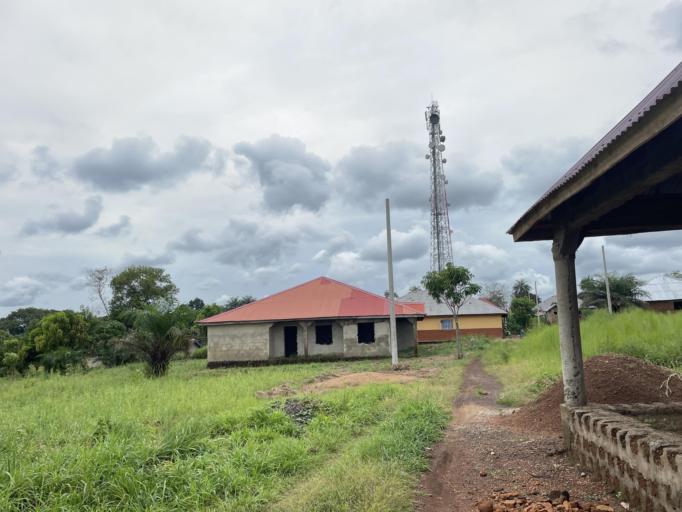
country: SL
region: Northern Province
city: Kambia
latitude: 9.1252
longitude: -12.9074
